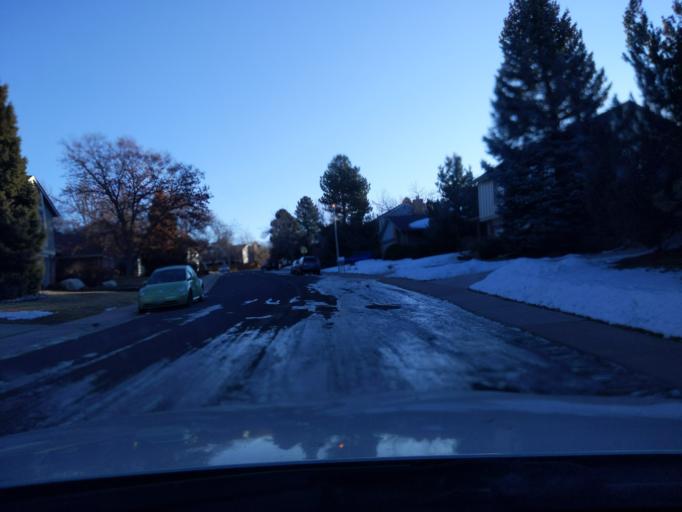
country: US
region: Colorado
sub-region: Arapahoe County
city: Centennial
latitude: 39.5729
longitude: -104.8897
